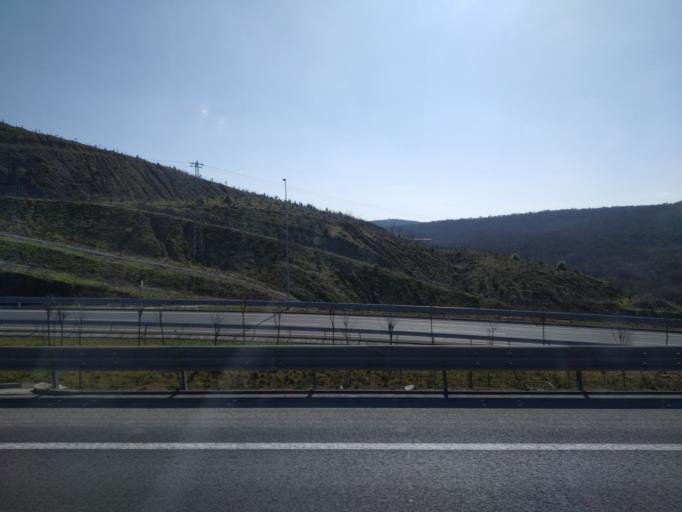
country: TR
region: Istanbul
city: Mahmut Sevket Pasa
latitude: 41.1908
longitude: 29.1975
